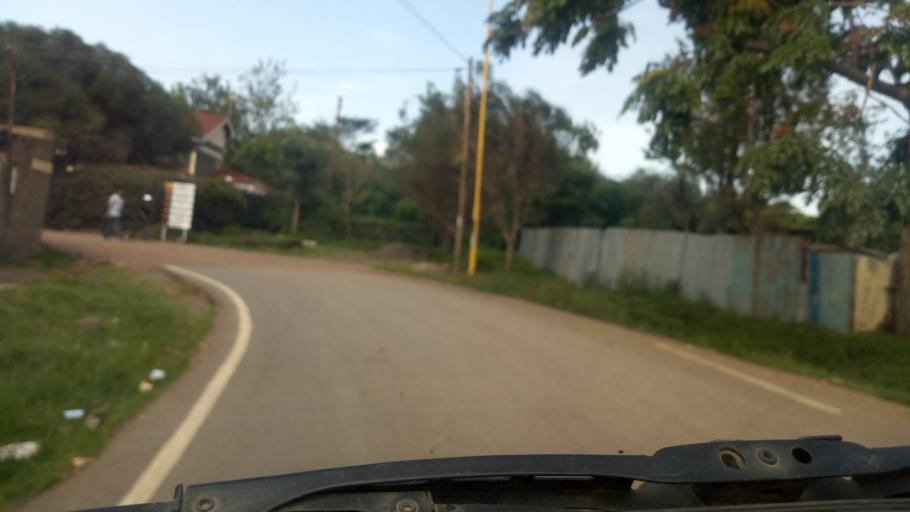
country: KE
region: Nakuru
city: Nakuru
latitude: -0.2785
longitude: 36.1037
